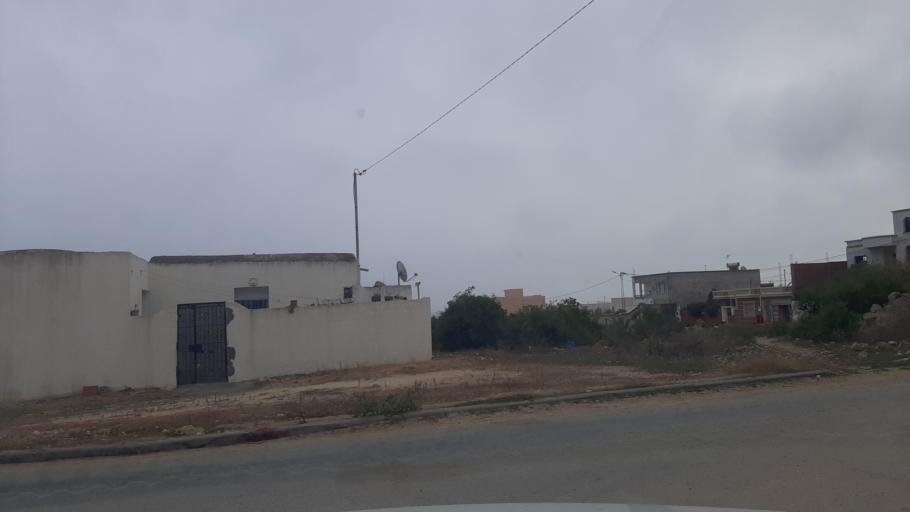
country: TN
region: Nabul
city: Menzel Heurr
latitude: 36.6835
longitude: 10.9281
